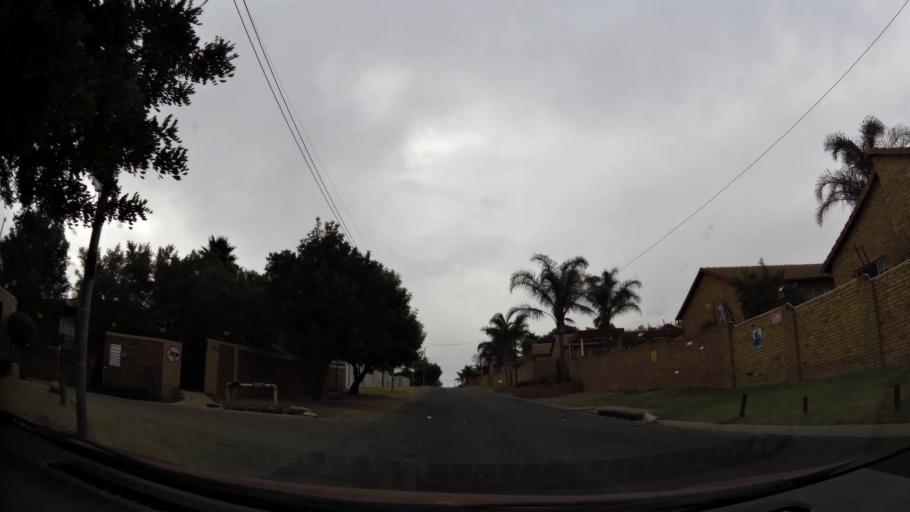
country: ZA
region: Gauteng
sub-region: City of Johannesburg Metropolitan Municipality
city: Roodepoort
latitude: -26.1094
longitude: 27.9045
